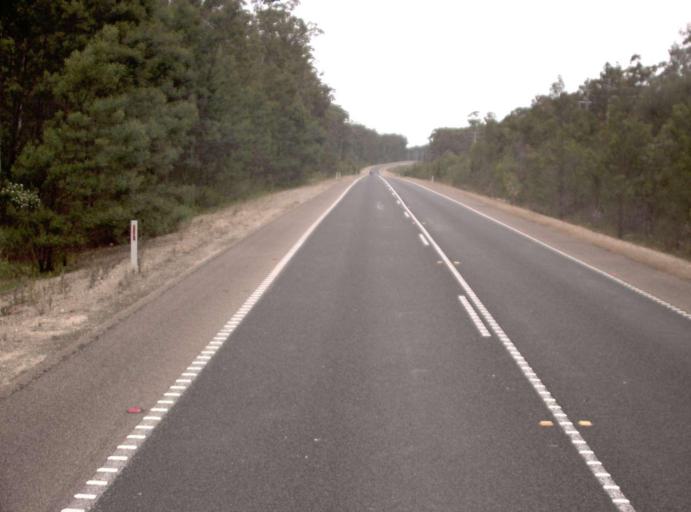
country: AU
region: Victoria
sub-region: East Gippsland
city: Lakes Entrance
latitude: -37.7082
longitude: 148.0698
